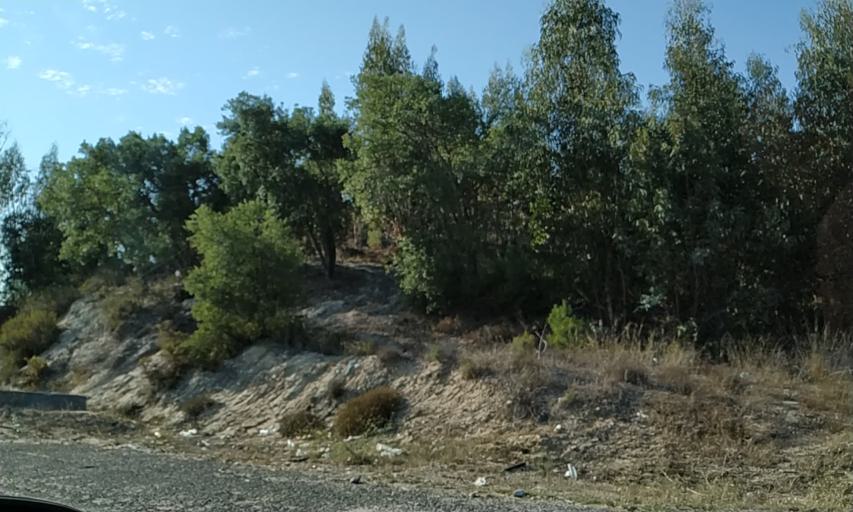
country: PT
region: Santarem
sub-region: Almeirim
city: Fazendas de Almeirim
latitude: 39.1159
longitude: -8.5917
